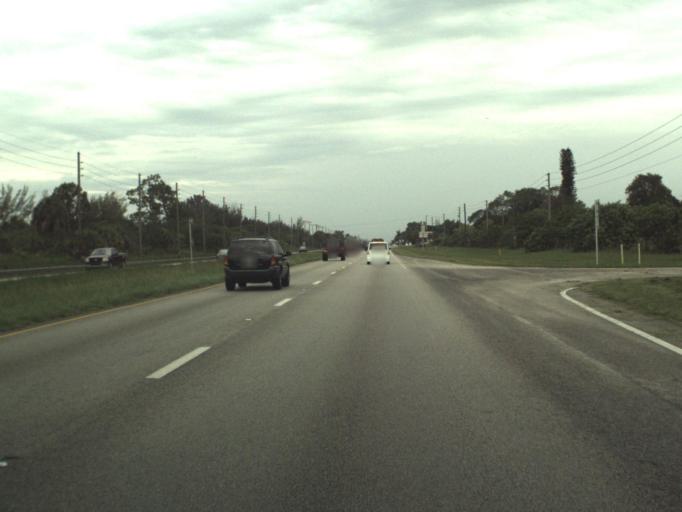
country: US
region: Florida
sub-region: Palm Beach County
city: Loxahatchee Groves
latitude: 26.6825
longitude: -80.2697
